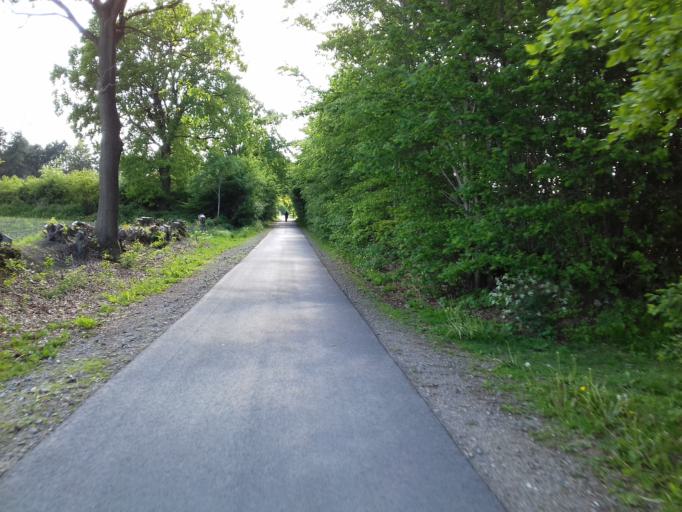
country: DE
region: Schleswig-Holstein
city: Bonebuttel
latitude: 54.0715
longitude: 10.0533
